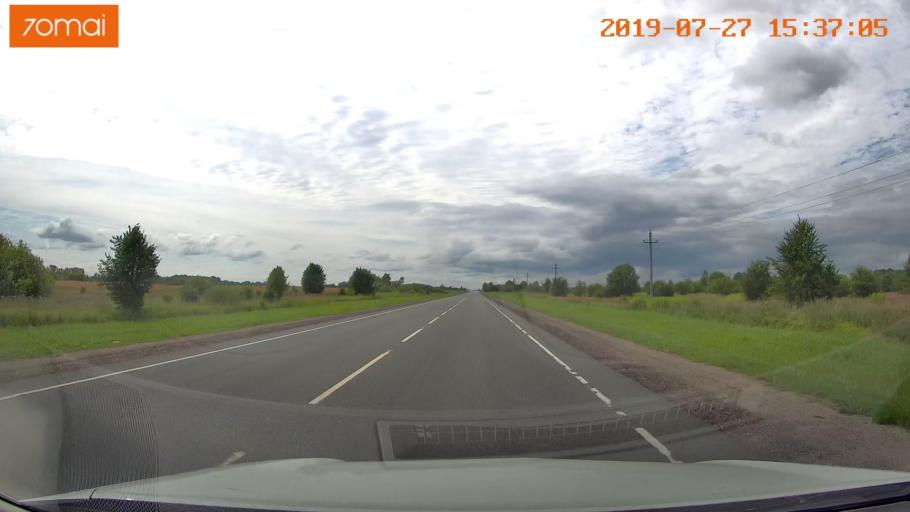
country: RU
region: Kaliningrad
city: Gusev
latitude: 54.6106
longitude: 22.3517
